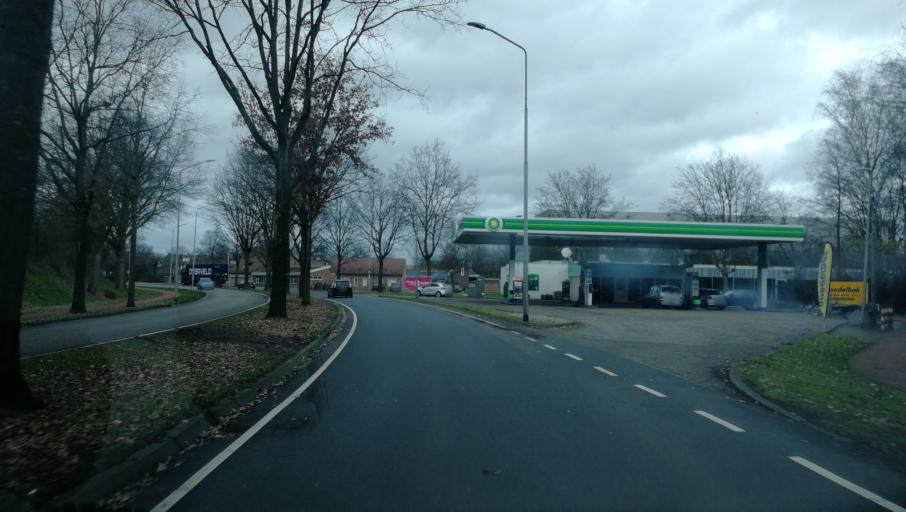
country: NL
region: Limburg
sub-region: Gemeente Venlo
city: Tegelen
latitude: 51.3722
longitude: 6.1362
